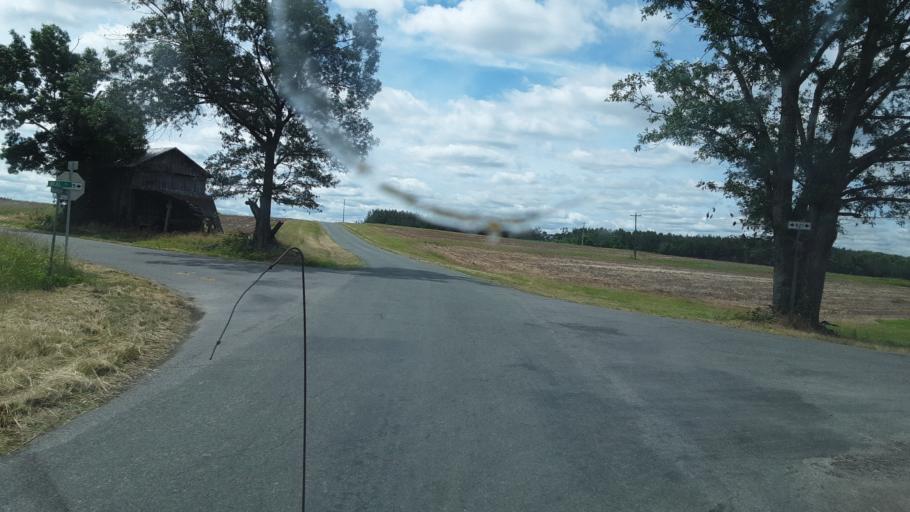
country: US
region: Virginia
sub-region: Pittsylvania County
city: Chatham
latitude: 36.8267
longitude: -79.4579
